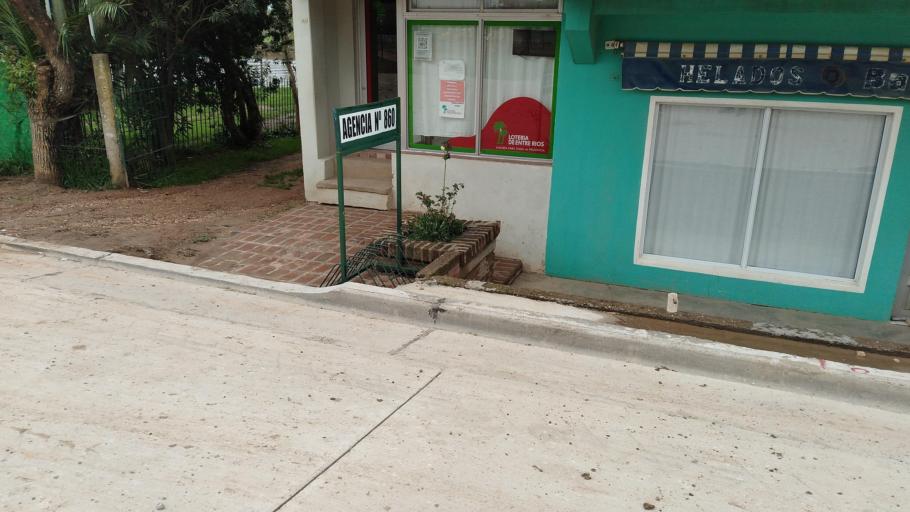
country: AR
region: Entre Rios
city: Villa Paranacito
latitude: -33.7162
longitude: -58.6625
